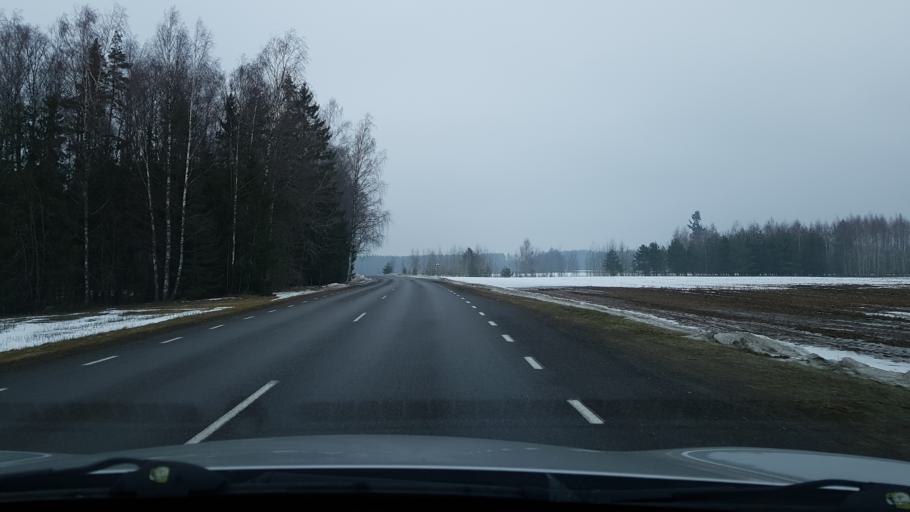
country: EE
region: Valgamaa
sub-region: Torva linn
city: Torva
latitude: 58.1028
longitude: 26.0108
